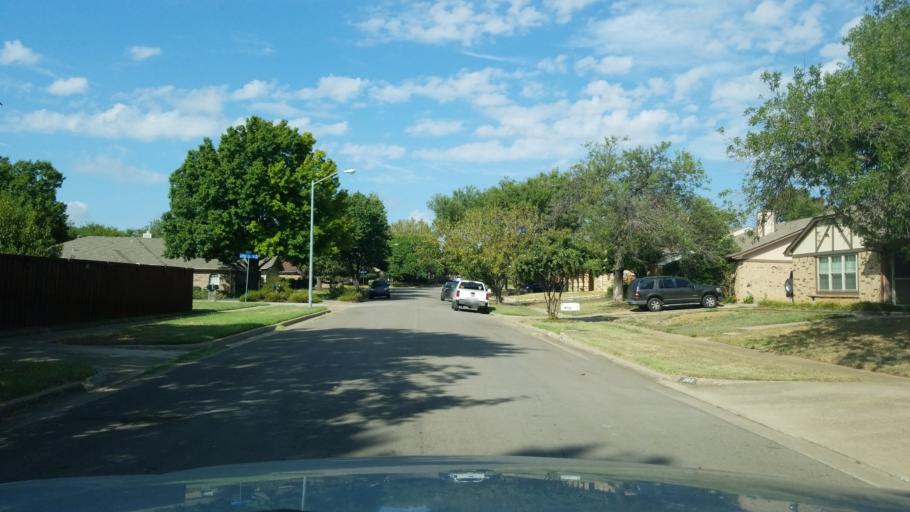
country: US
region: Texas
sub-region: Tarrant County
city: Euless
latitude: 32.8488
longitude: -97.0805
